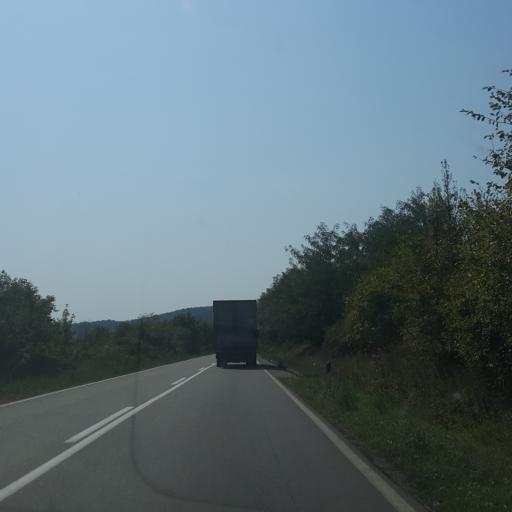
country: RS
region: Central Serbia
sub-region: Zajecarski Okrug
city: Zajecar
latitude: 43.8240
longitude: 22.2879
